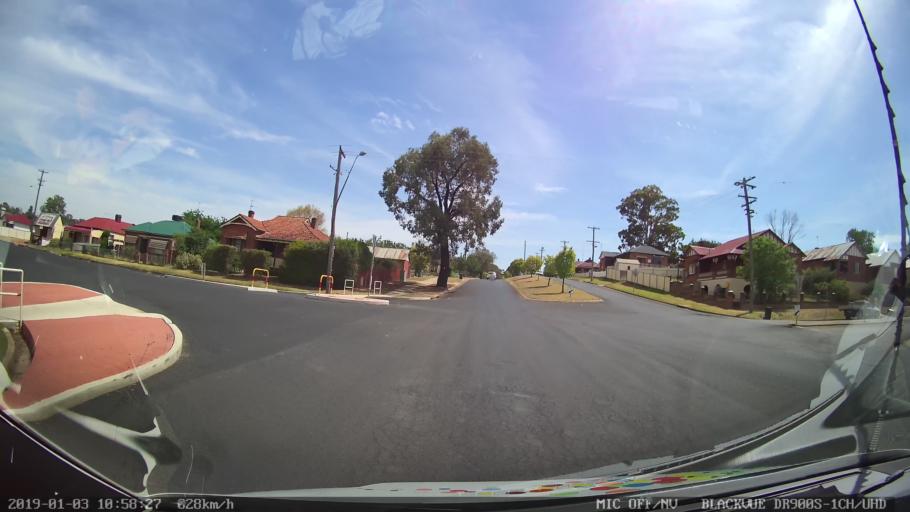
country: AU
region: New South Wales
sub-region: Young
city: Young
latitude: -34.3107
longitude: 148.2961
